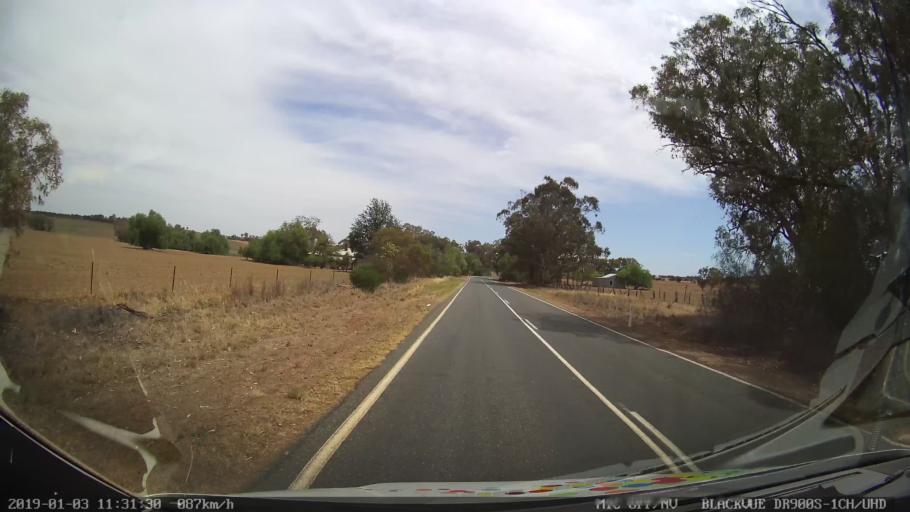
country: AU
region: New South Wales
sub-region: Weddin
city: Grenfell
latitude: -33.9697
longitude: 148.1830
